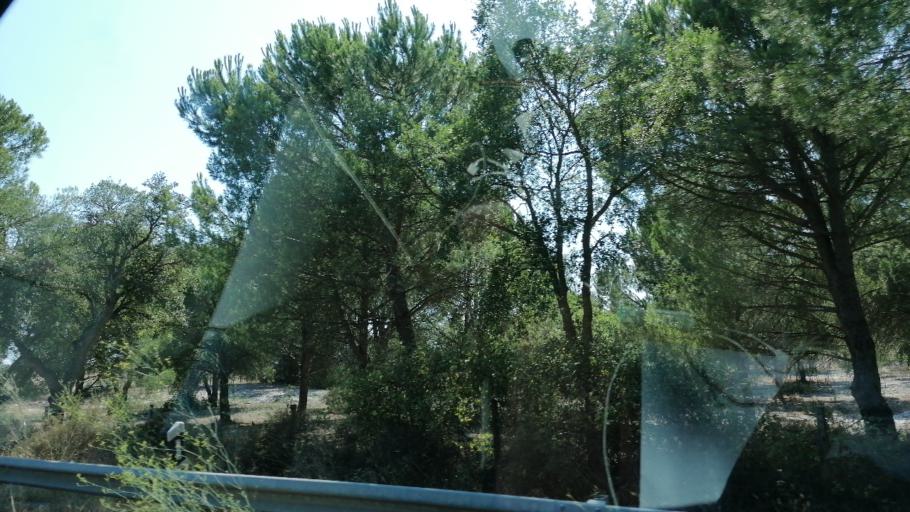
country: PT
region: Evora
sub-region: Vendas Novas
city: Vendas Novas
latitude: 38.7064
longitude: -8.6139
